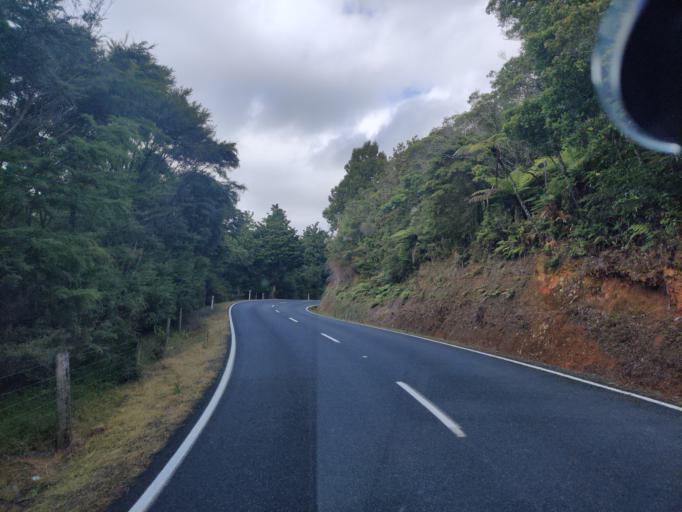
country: NZ
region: Northland
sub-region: Whangarei
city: Ngunguru
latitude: -35.5789
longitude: 174.4117
